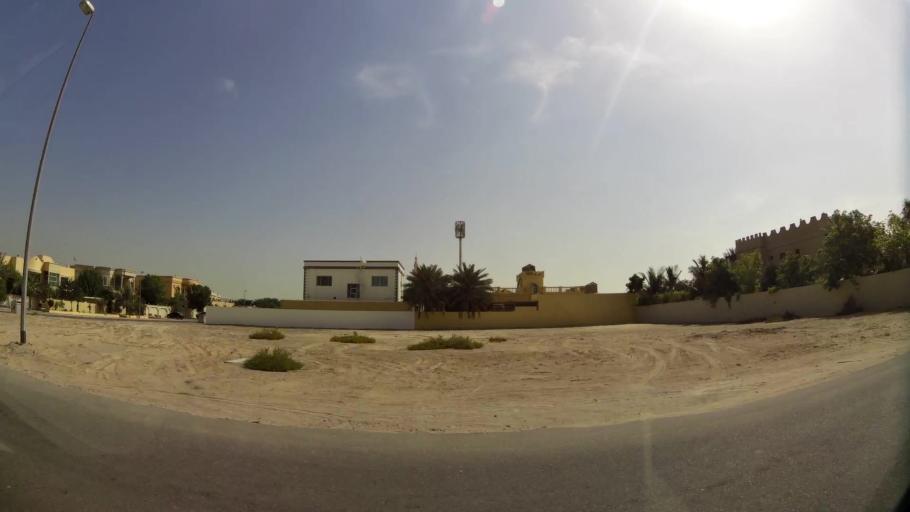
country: AE
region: Ash Shariqah
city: Sharjah
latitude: 25.2686
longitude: 55.4100
